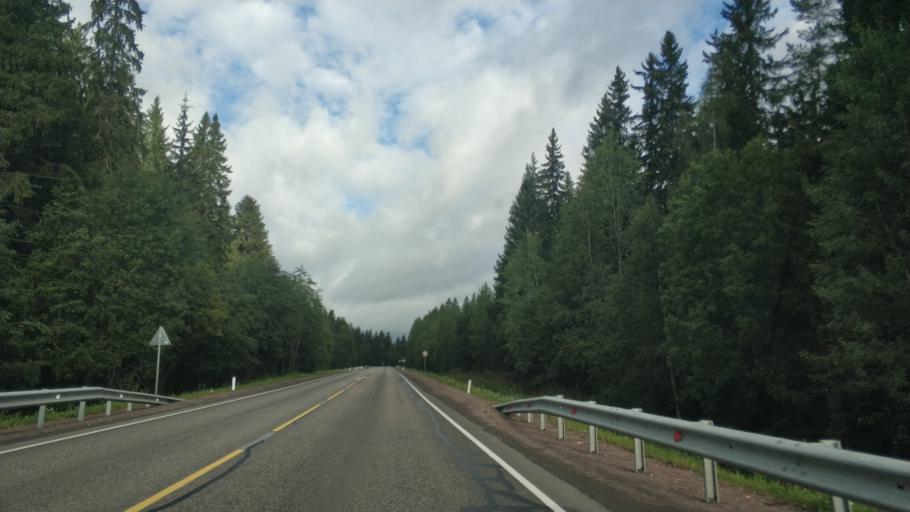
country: RU
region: Republic of Karelia
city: Khelyulya
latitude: 61.7859
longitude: 30.6406
